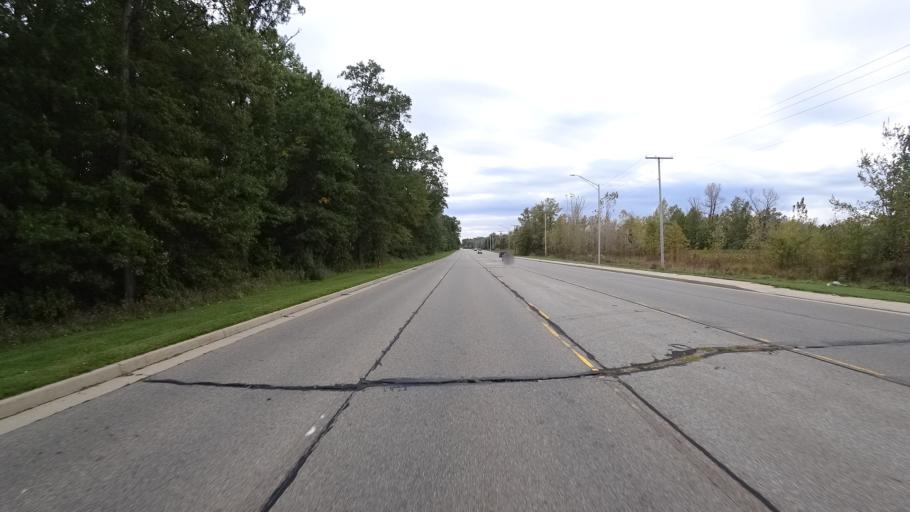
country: US
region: Indiana
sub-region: LaPorte County
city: Trail Creek
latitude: 41.6717
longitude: -86.8845
